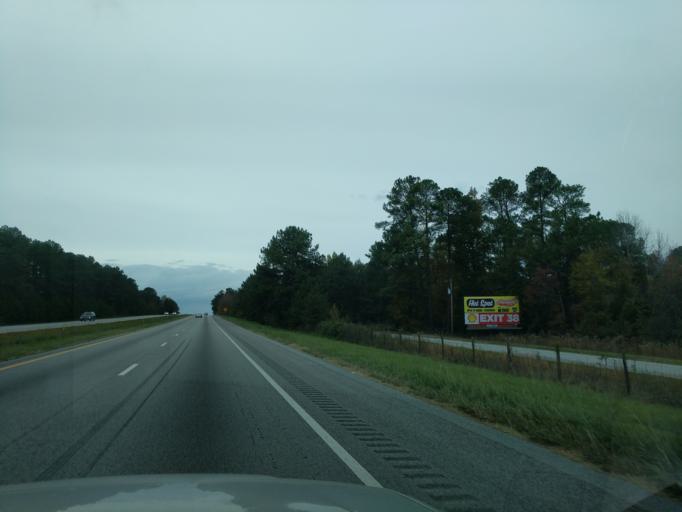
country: US
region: South Carolina
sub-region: Laurens County
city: Joanna
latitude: 34.4650
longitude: -81.8012
